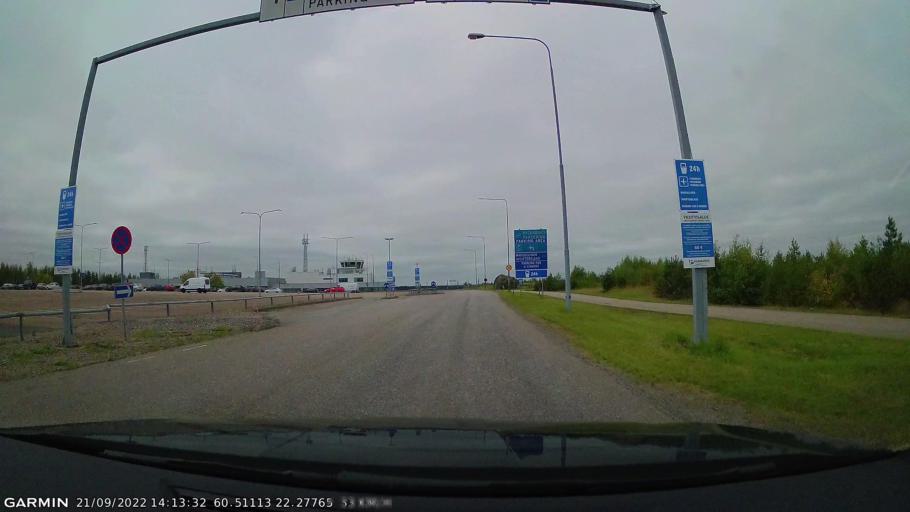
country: FI
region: Varsinais-Suomi
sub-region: Turku
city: Turku
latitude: 60.5110
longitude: 22.2778
